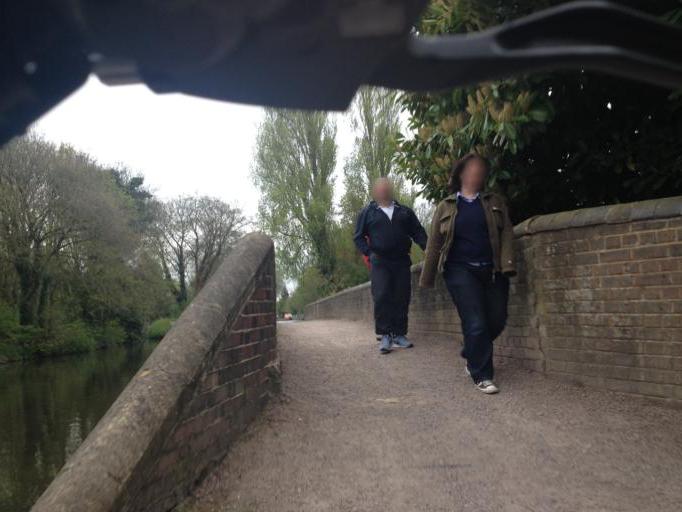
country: GB
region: England
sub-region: Greater London
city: Harefield
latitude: 51.6049
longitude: -0.4974
